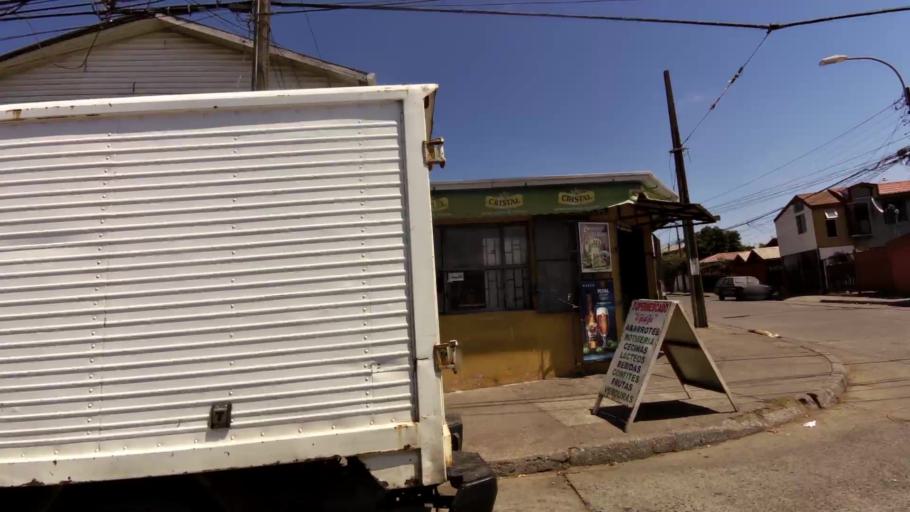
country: CL
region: Biobio
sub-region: Provincia de Concepcion
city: Concepcion
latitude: -36.8076
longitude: -73.0435
